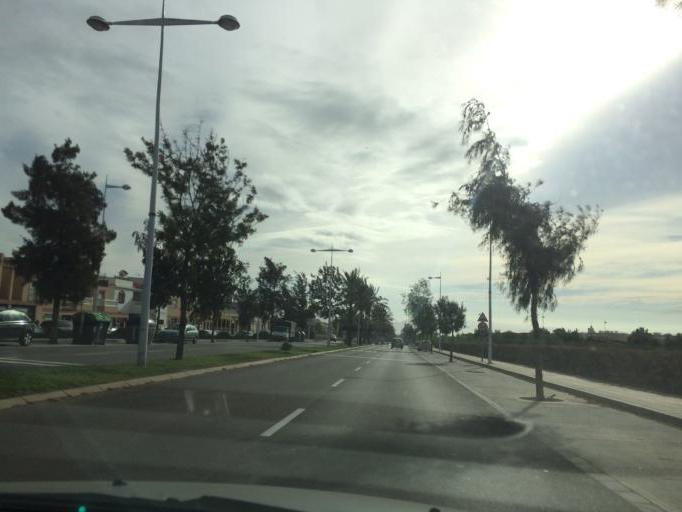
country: ES
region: Andalusia
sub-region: Provincia de Almeria
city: Retamar
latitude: 36.8504
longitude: -2.3107
